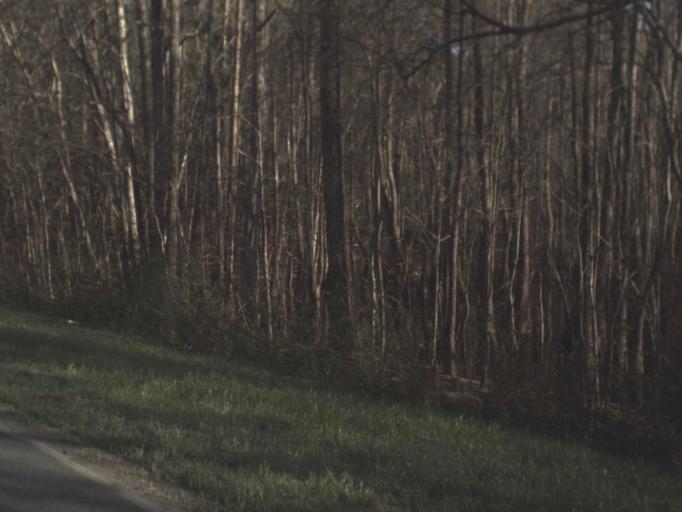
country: US
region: Florida
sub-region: Jackson County
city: Marianna
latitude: 30.7405
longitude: -85.1257
